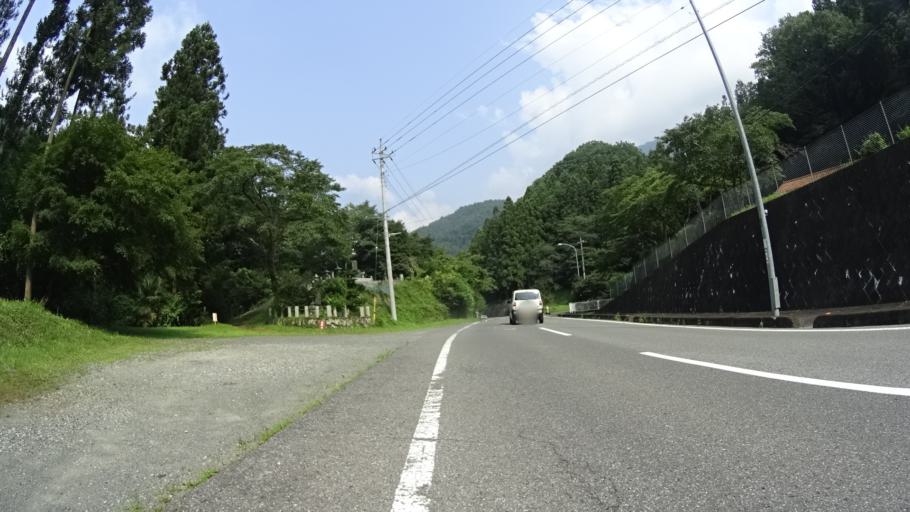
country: JP
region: Saitama
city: Chichibu
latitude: 36.0358
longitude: 138.9184
